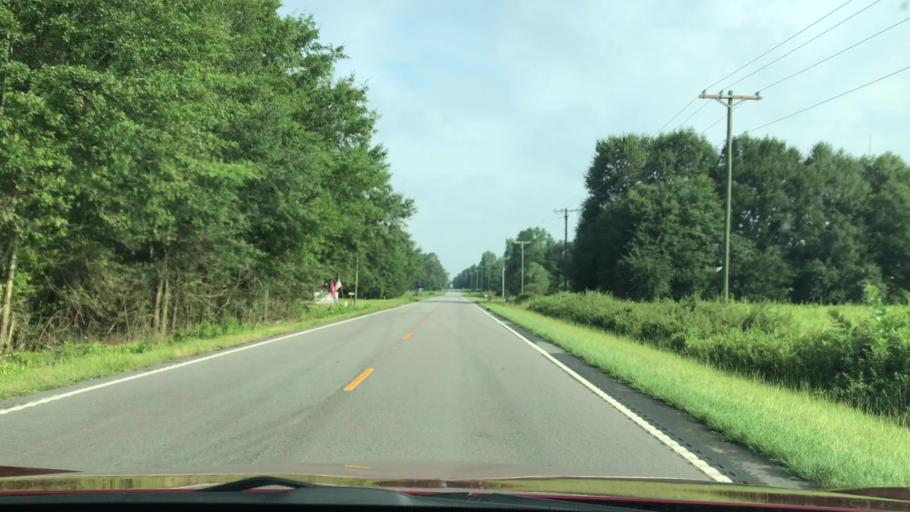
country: US
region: South Carolina
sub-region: Lexington County
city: Batesburg-Leesville
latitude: 33.7164
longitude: -81.4994
